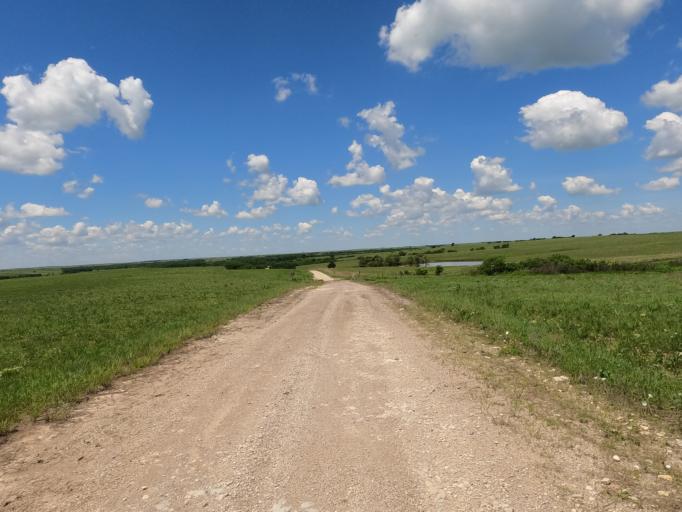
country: US
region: Kansas
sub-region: Marion County
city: Marion
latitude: 38.2419
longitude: -96.7943
